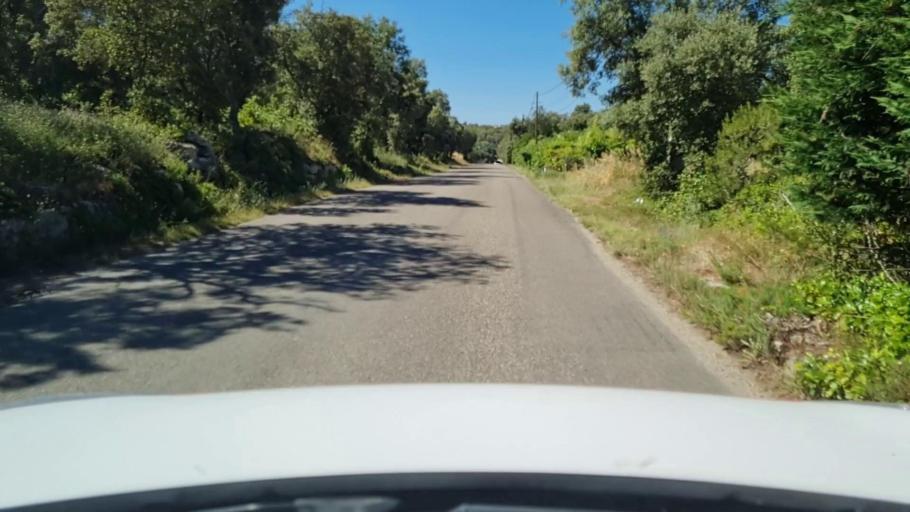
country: FR
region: Languedoc-Roussillon
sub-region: Departement du Gard
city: Villevieille
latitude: 43.7815
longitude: 4.1200
